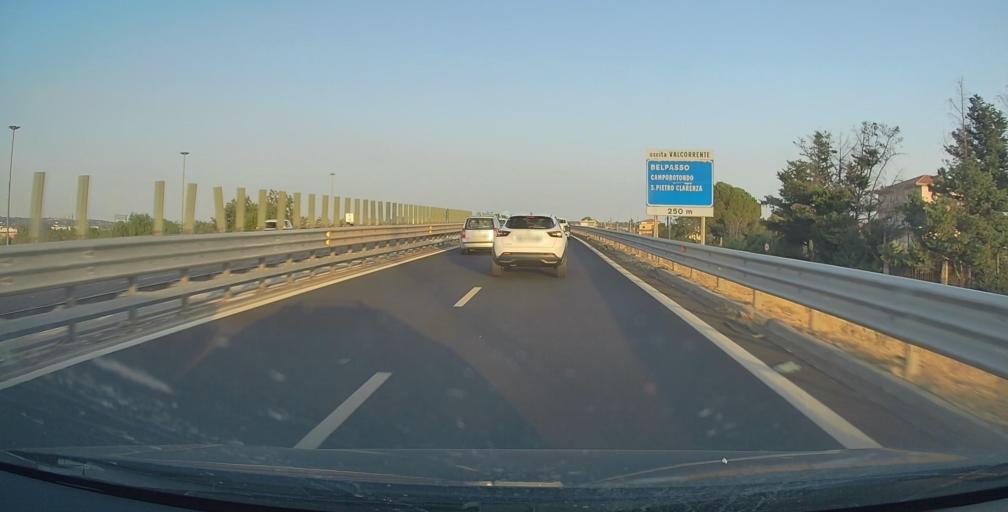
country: IT
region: Sicily
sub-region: Catania
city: Motta Sant'Anastasia
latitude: 37.5414
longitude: 14.9547
